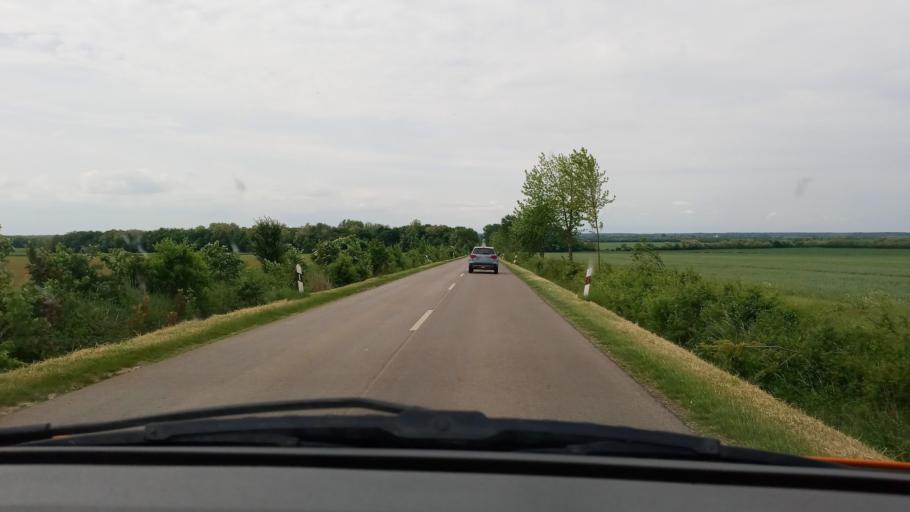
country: HU
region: Baranya
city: Vajszlo
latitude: 45.9311
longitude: 18.0666
